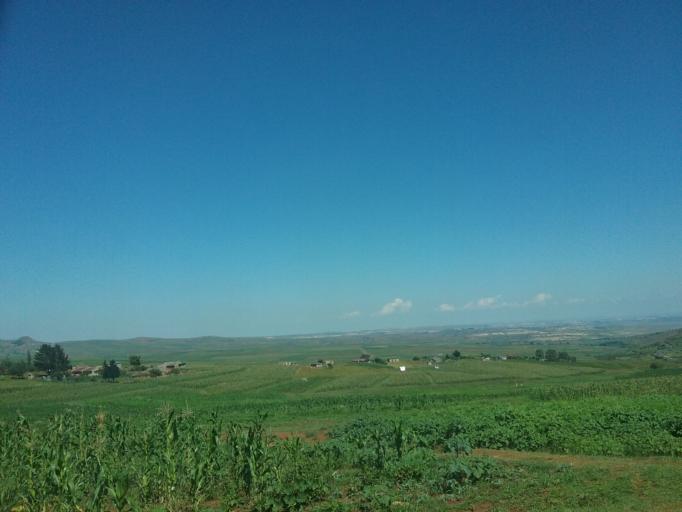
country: LS
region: Berea
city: Teyateyaneng
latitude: -29.2251
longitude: 27.8683
